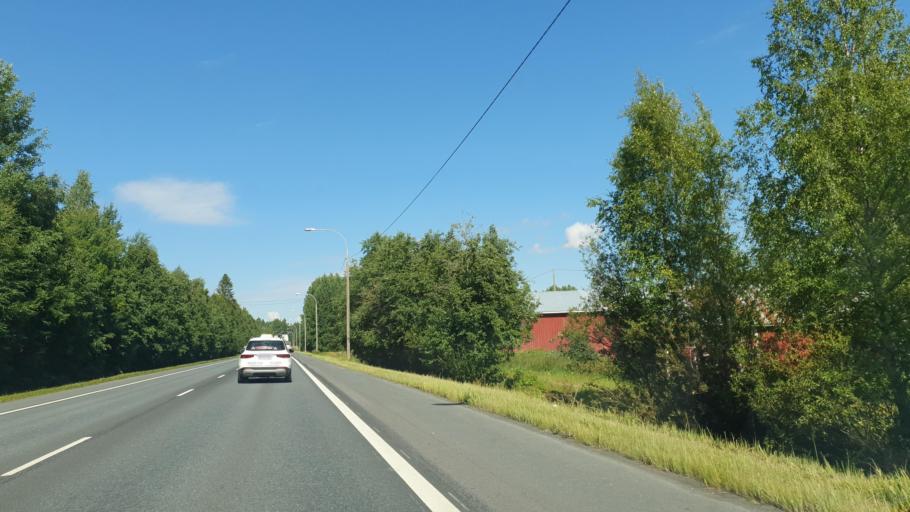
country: FI
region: Northern Savo
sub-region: Ylae-Savo
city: Iisalmi
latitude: 63.5015
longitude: 27.2634
